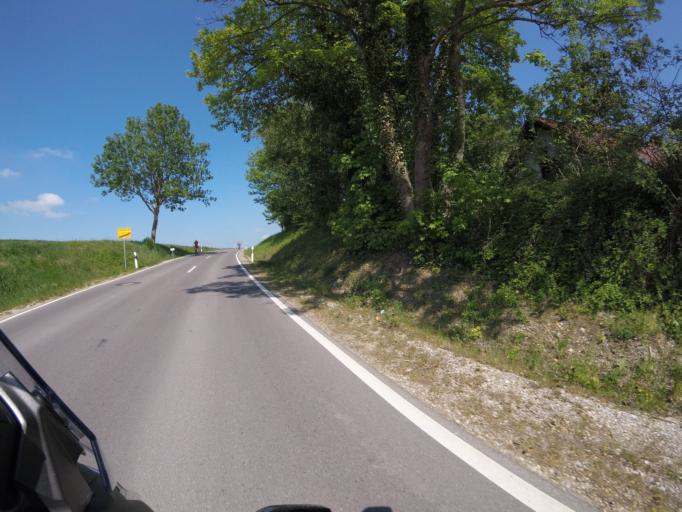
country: DE
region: Bavaria
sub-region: Upper Bavaria
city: Fahrenzhausen
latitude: 48.3458
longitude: 11.5773
